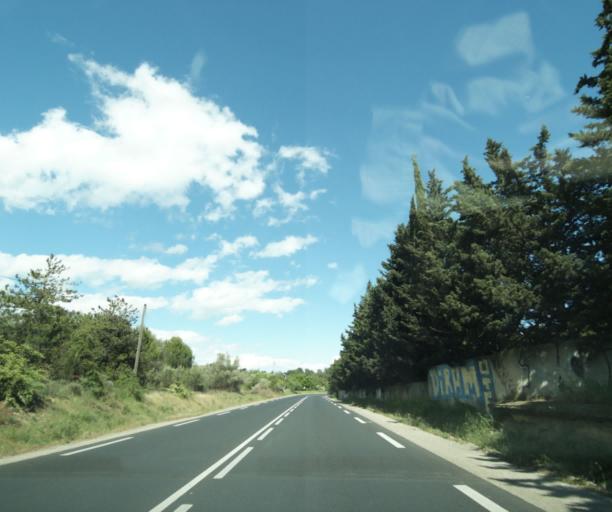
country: FR
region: Languedoc-Roussillon
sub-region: Departement de l'Herault
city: Saint-Jean-de-Vedas
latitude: 43.5870
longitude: 3.8310
